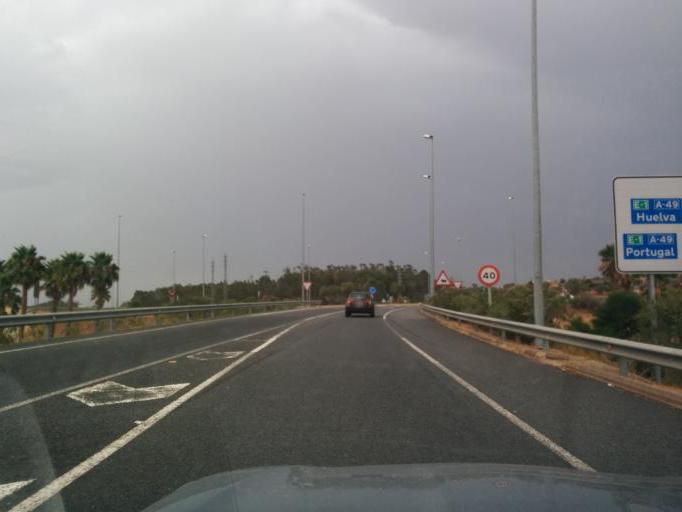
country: ES
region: Andalusia
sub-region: Provincia de Huelva
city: Ayamonte
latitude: 37.2387
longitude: -7.3795
